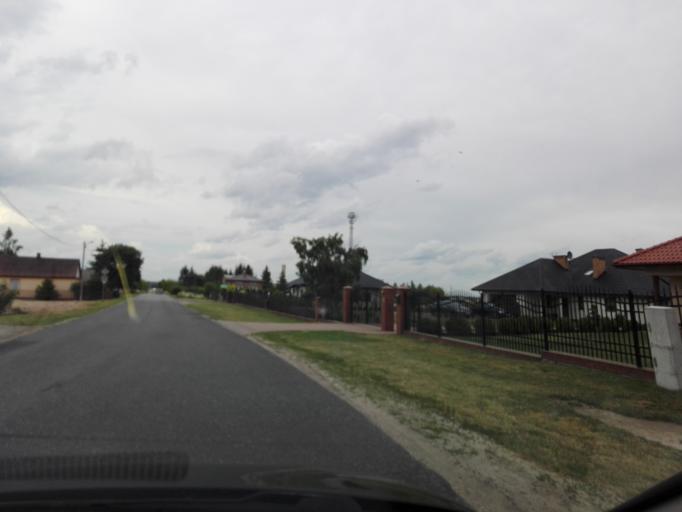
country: PL
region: Lublin Voivodeship
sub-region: Powiat pulawski
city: Kurow
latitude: 51.3965
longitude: 22.1980
